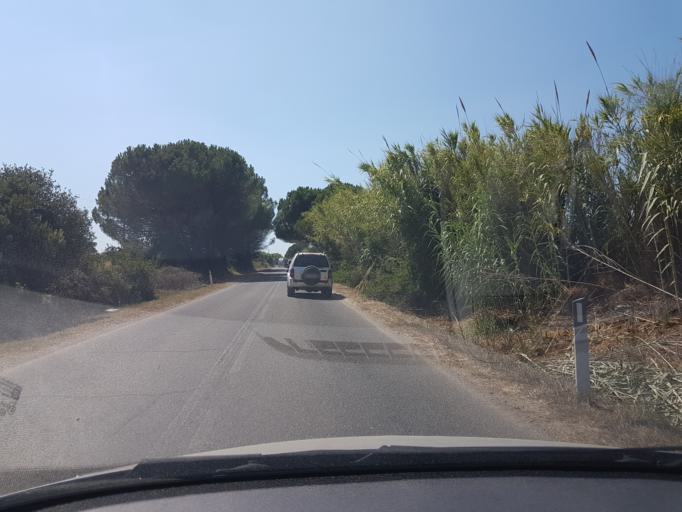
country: IT
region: Sardinia
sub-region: Provincia di Oristano
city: Riola Sardo
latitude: 40.0009
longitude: 8.5244
